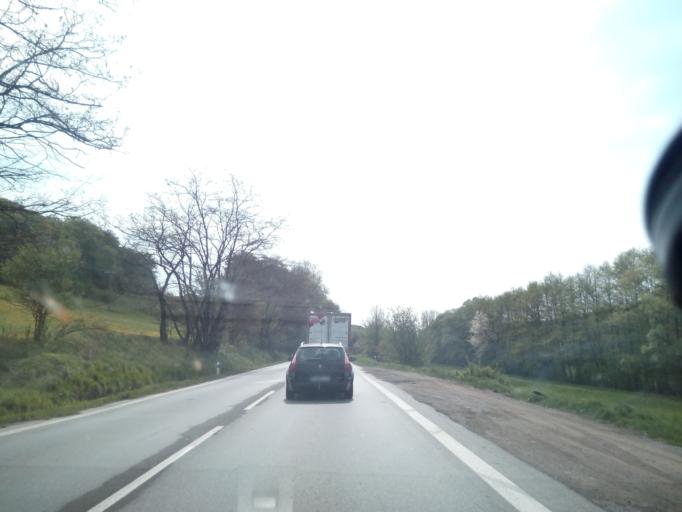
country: SK
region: Presovsky
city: Giraltovce
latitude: 49.0485
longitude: 21.4362
